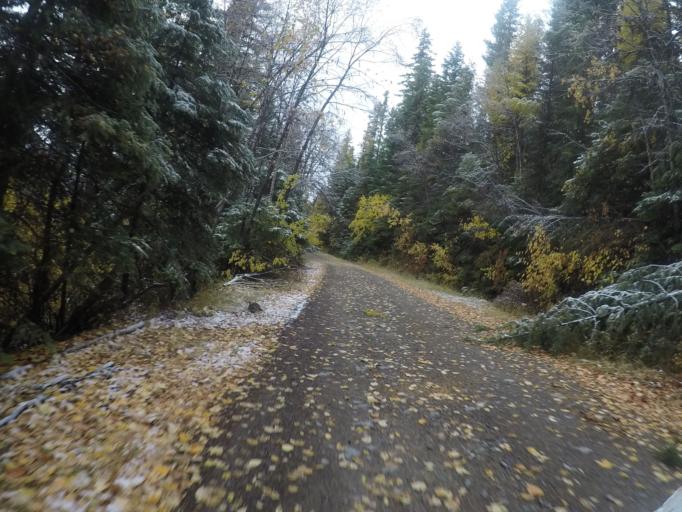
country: US
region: Montana
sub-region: Flathead County
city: Bigfork
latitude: 47.8879
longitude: -113.8755
